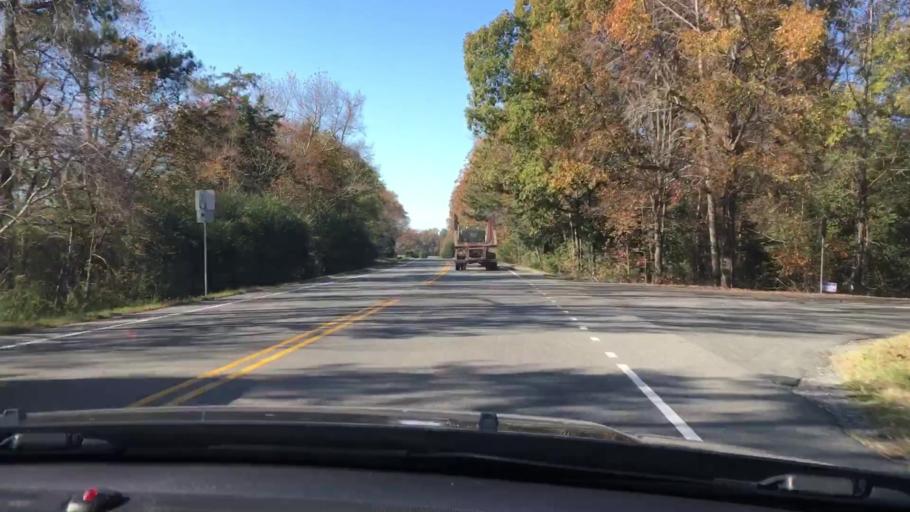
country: US
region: Virginia
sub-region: King William County
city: Central Garage
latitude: 37.7748
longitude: -77.1586
